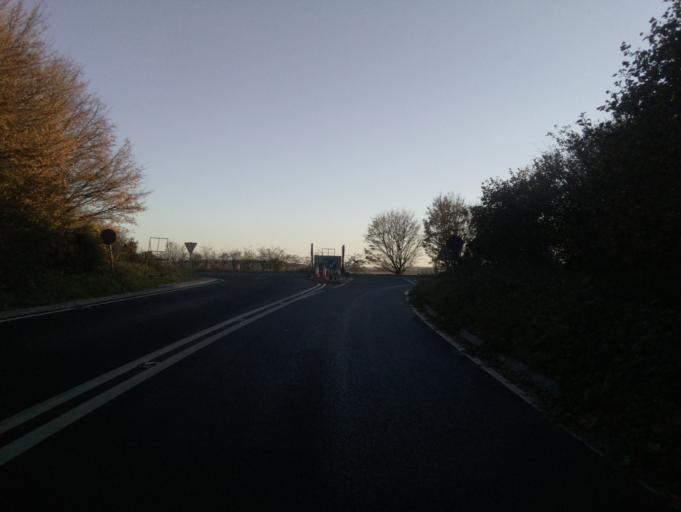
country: GB
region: England
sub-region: Wiltshire
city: Chicklade
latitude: 51.1056
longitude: -2.1643
